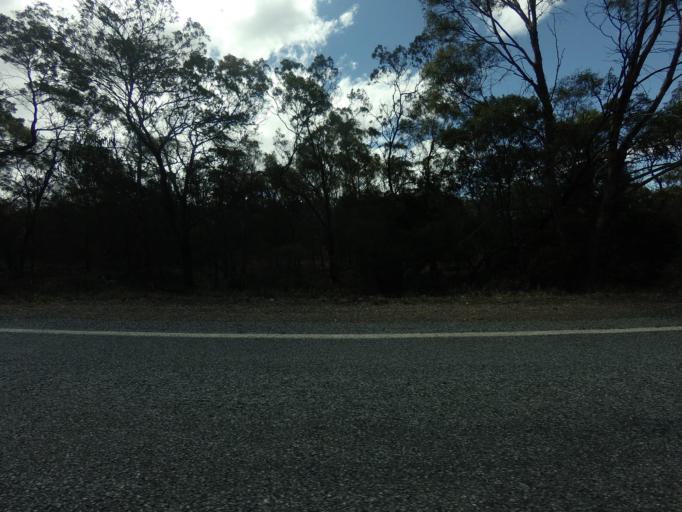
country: AU
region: Tasmania
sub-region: Break O'Day
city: St Helens
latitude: -42.0163
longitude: 148.0036
